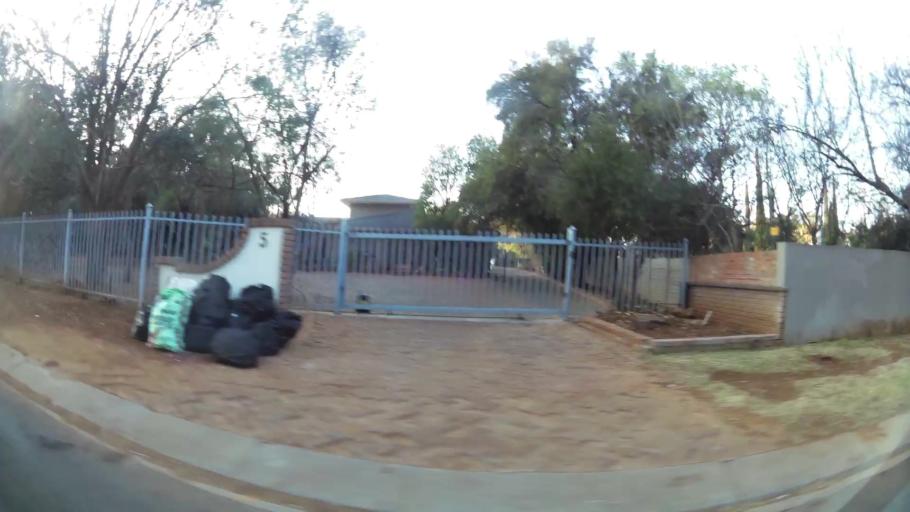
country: ZA
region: Orange Free State
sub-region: Mangaung Metropolitan Municipality
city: Bloemfontein
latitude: -29.0836
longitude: 26.1573
